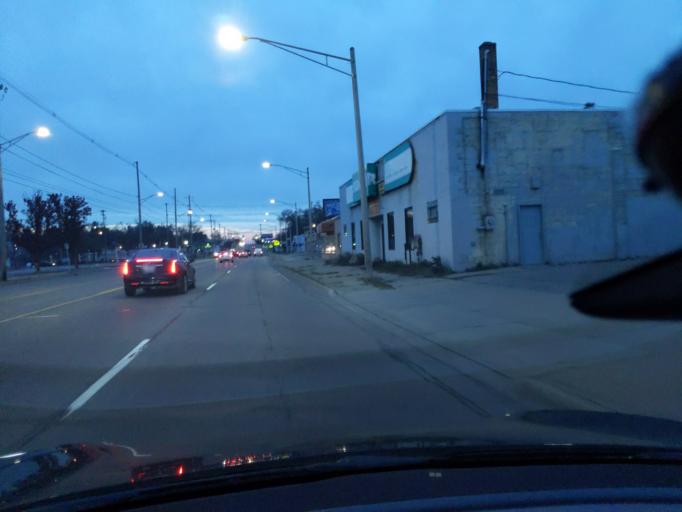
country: US
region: Michigan
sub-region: Ingham County
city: Lansing
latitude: 42.6959
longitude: -84.5480
